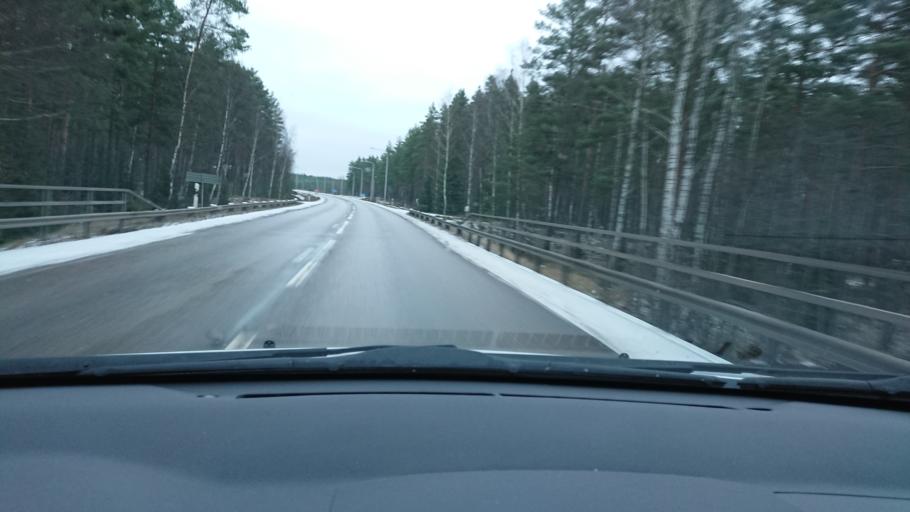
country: SE
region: Kalmar
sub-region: Hultsfreds Kommun
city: Hultsfred
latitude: 57.5149
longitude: 15.8409
